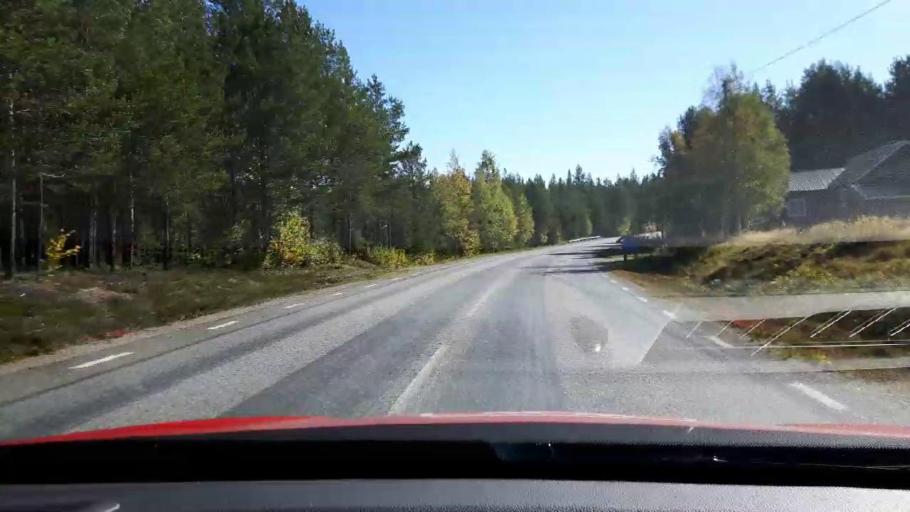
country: SE
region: Jaemtland
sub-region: Harjedalens Kommun
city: Sveg
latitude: 62.3629
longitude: 14.0011
